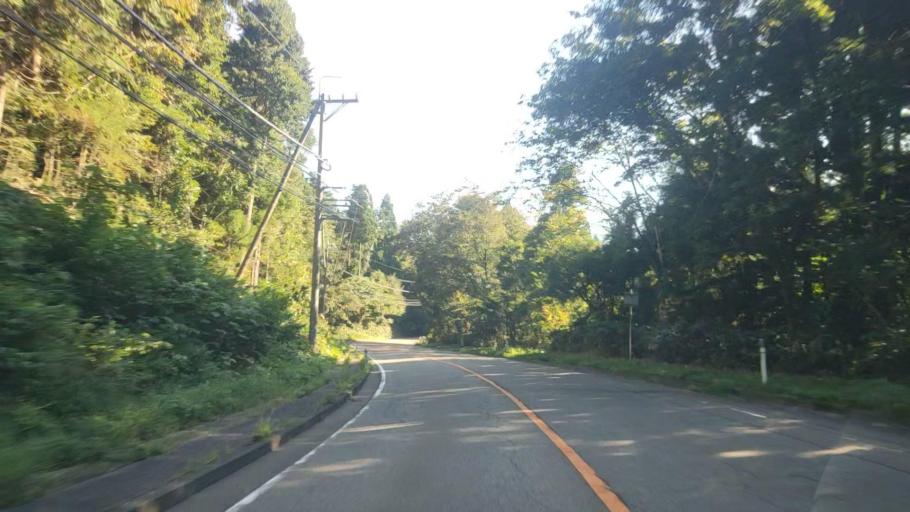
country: JP
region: Ishikawa
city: Nanao
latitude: 37.1278
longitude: 136.8633
